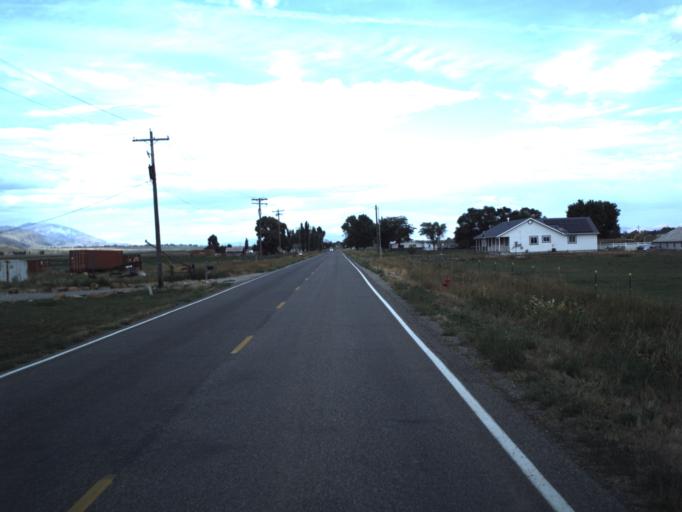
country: US
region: Utah
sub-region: Cache County
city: Lewiston
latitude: 41.9646
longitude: -111.9540
